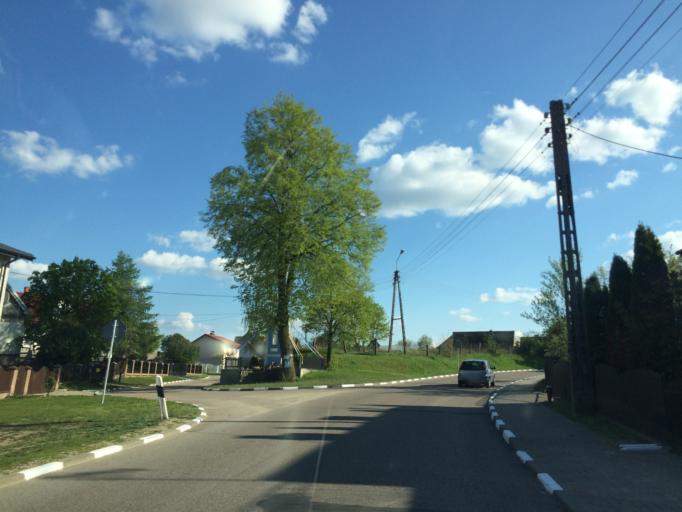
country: PL
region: Warmian-Masurian Voivodeship
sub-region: Powiat dzialdowski
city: Lidzbark
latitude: 53.2950
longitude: 19.8622
